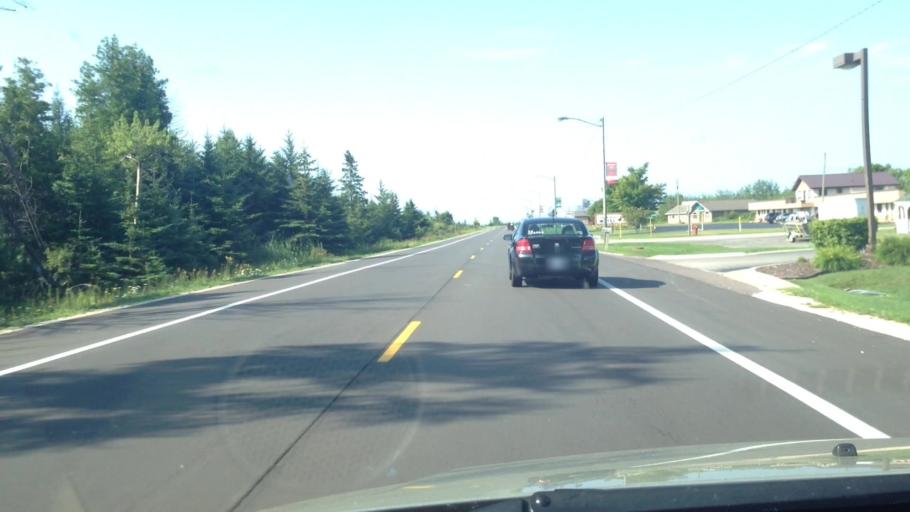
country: US
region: Michigan
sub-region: Schoolcraft County
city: Manistique
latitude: 45.9520
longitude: -86.2279
